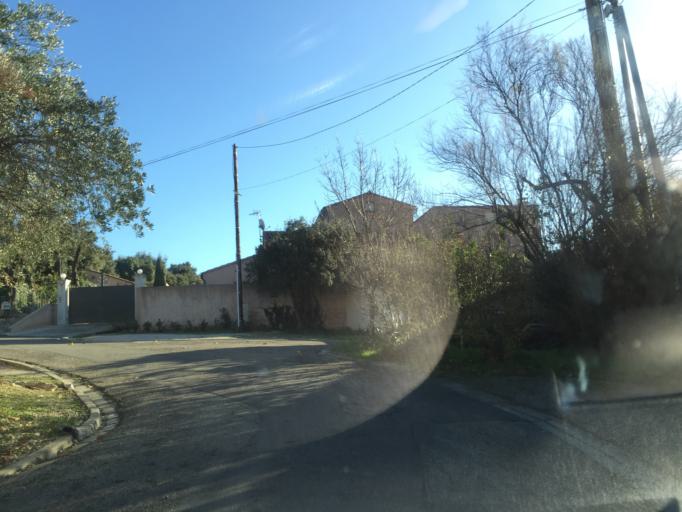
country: FR
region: Provence-Alpes-Cote d'Azur
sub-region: Departement du Vaucluse
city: Bedarrides
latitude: 44.0348
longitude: 4.8932
